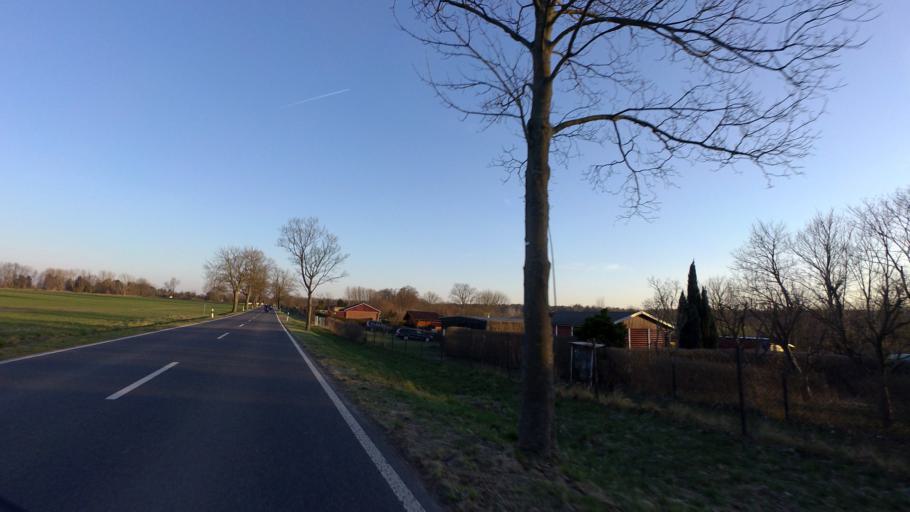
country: DE
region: Berlin
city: Hellersdorf
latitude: 52.5669
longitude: 13.6255
